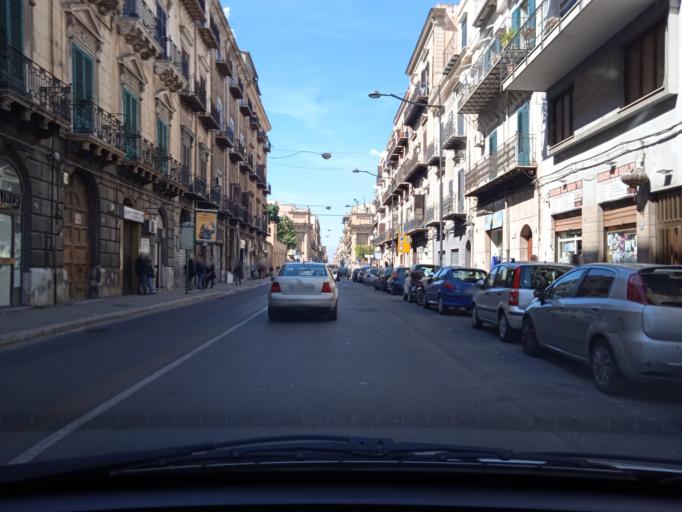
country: IT
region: Sicily
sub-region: Palermo
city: Palermo
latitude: 38.1089
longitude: 13.3658
